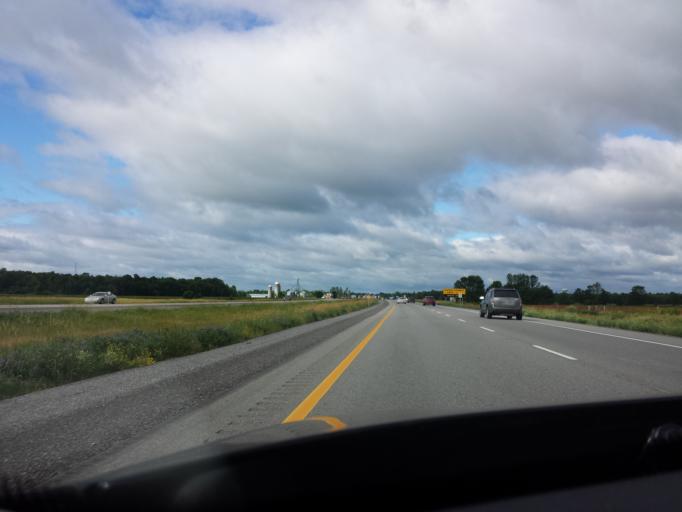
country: CA
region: Ontario
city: Carleton Place
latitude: 45.1471
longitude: -76.0968
